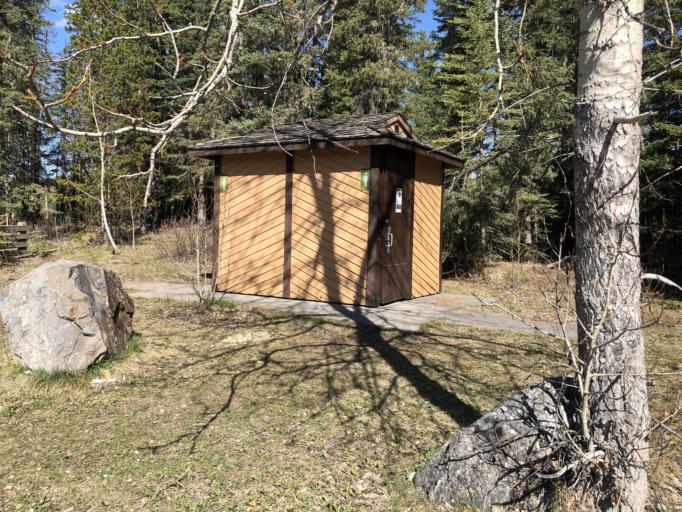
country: CA
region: Alberta
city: Cochrane
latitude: 51.0328
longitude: -114.8095
